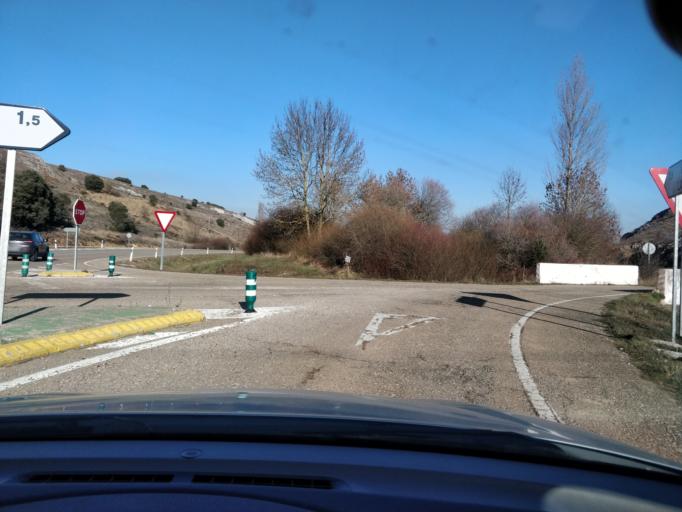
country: ES
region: Castille and Leon
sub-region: Provincia de Burgos
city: Quintanaortuno
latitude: 42.5159
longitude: -3.6936
